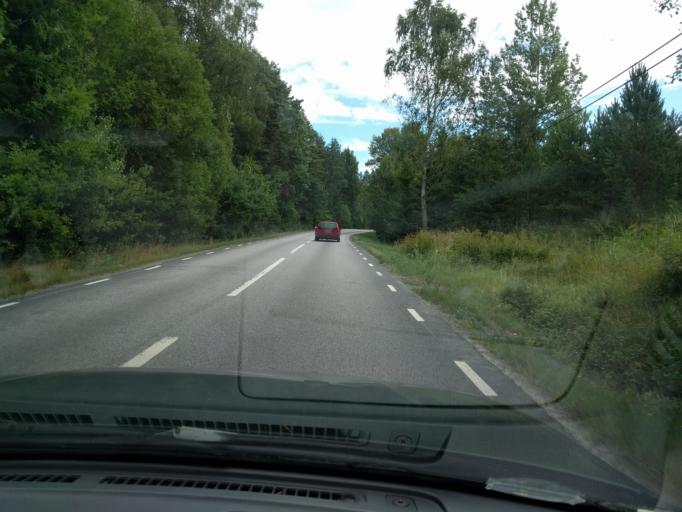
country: SE
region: Soedermanland
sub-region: Nykopings Kommun
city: Svalsta
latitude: 58.5188
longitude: 16.8011
